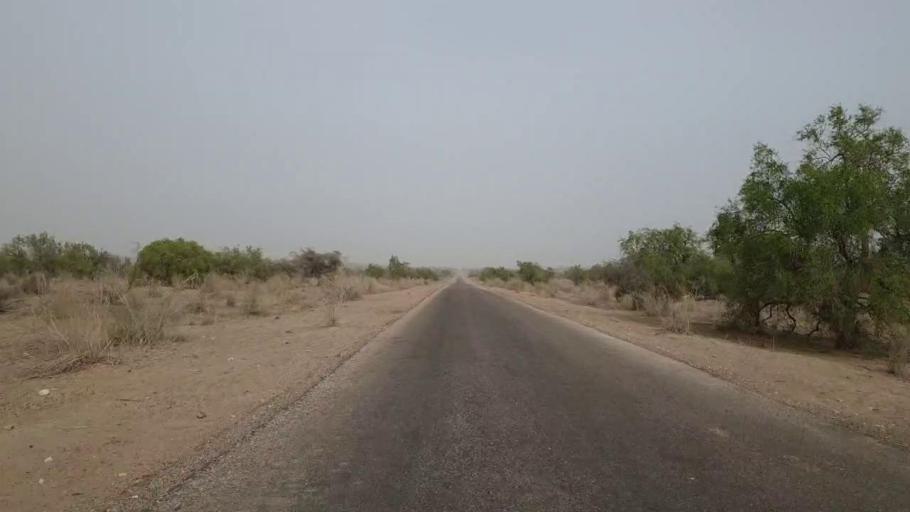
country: PK
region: Sindh
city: Islamkot
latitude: 24.5685
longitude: 70.3259
